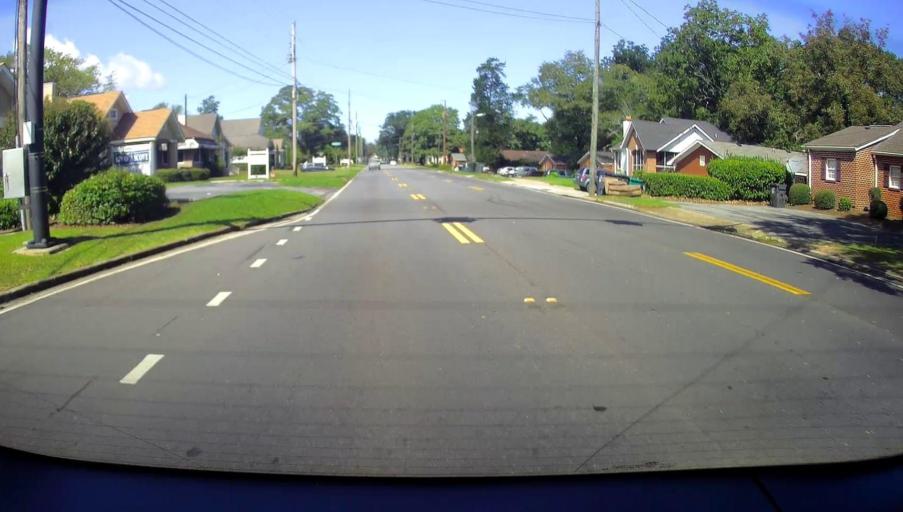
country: US
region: Georgia
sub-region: Bibb County
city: Macon
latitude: 32.8565
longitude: -83.6812
